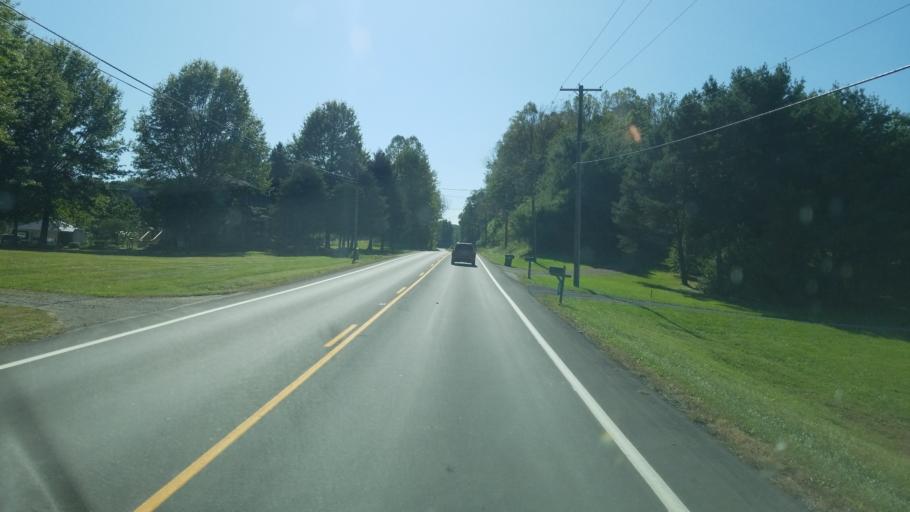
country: US
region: Ohio
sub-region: Stark County
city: Navarre
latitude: 40.6773
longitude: -81.5354
